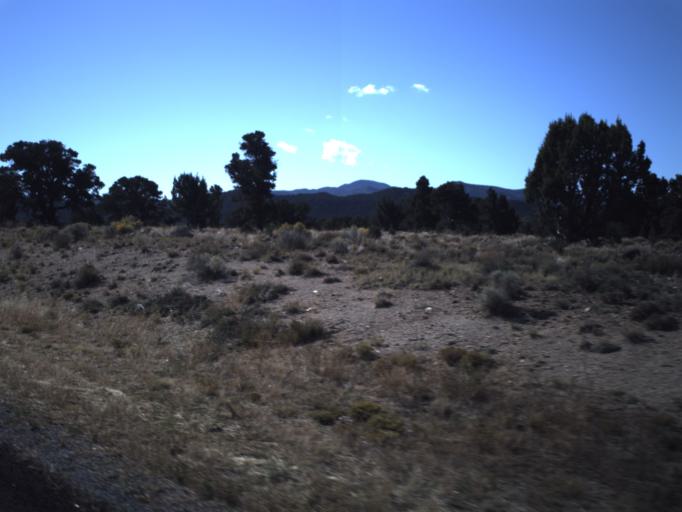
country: US
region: Utah
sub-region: Washington County
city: Enterprise
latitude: 37.6273
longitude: -113.4226
